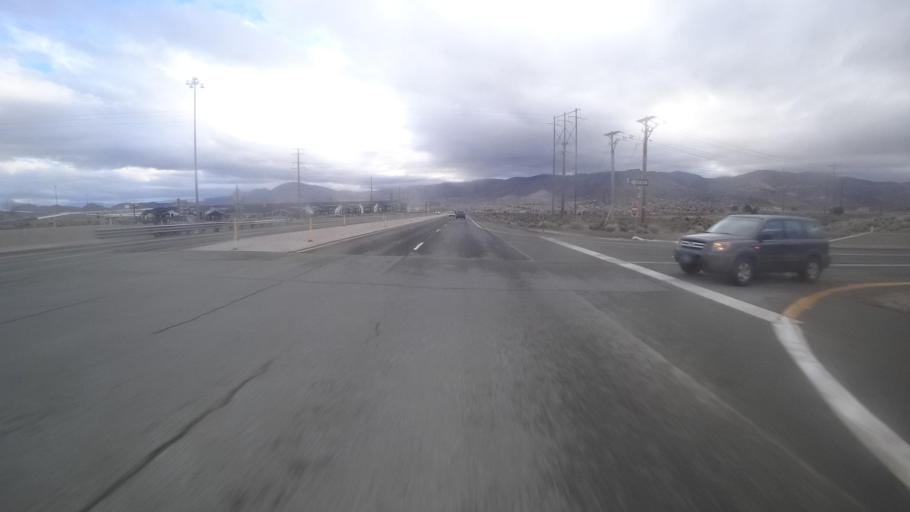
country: US
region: Nevada
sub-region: Washoe County
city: Sparks
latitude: 39.3975
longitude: -119.7569
